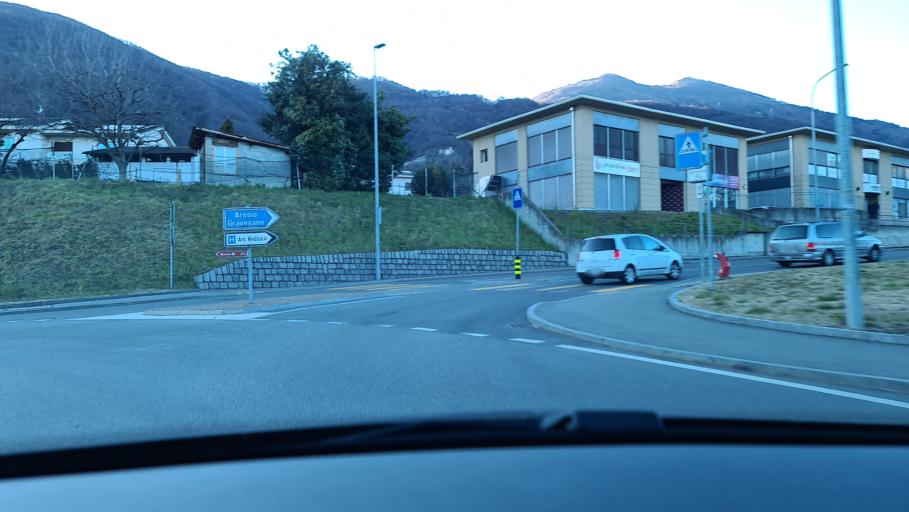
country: CH
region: Ticino
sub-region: Lugano District
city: Gravesano
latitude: 46.0358
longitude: 8.9244
